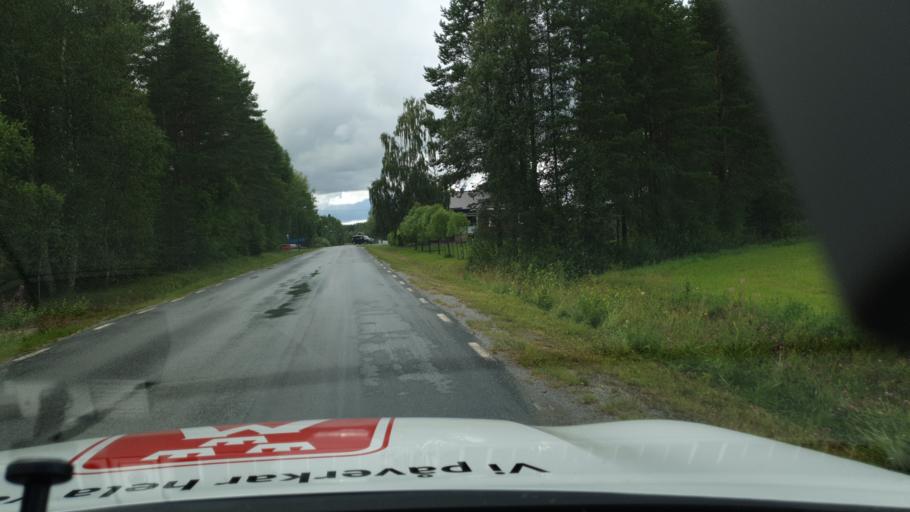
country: SE
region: Vaesterbotten
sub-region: Skelleftea Kommun
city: Viken
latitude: 64.5843
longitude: 20.9658
